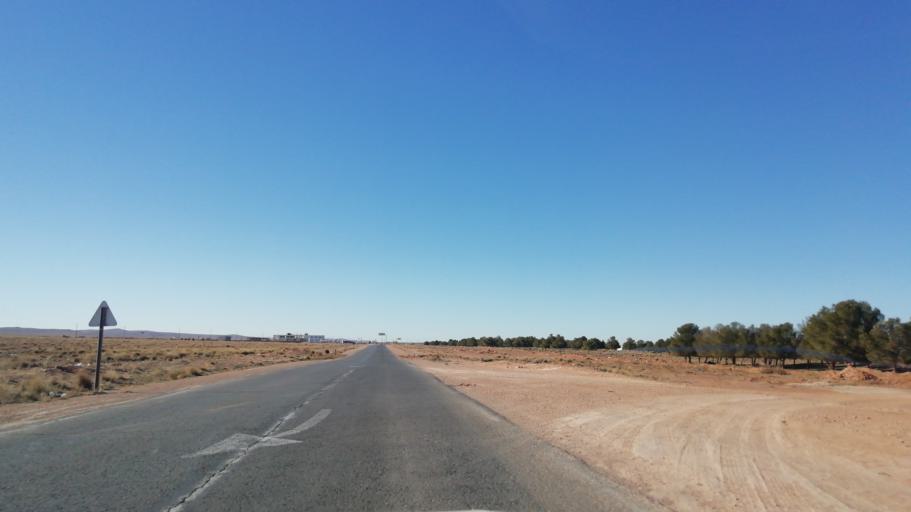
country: DZ
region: El Bayadh
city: El Bayadh
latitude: 33.6615
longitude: 0.9129
